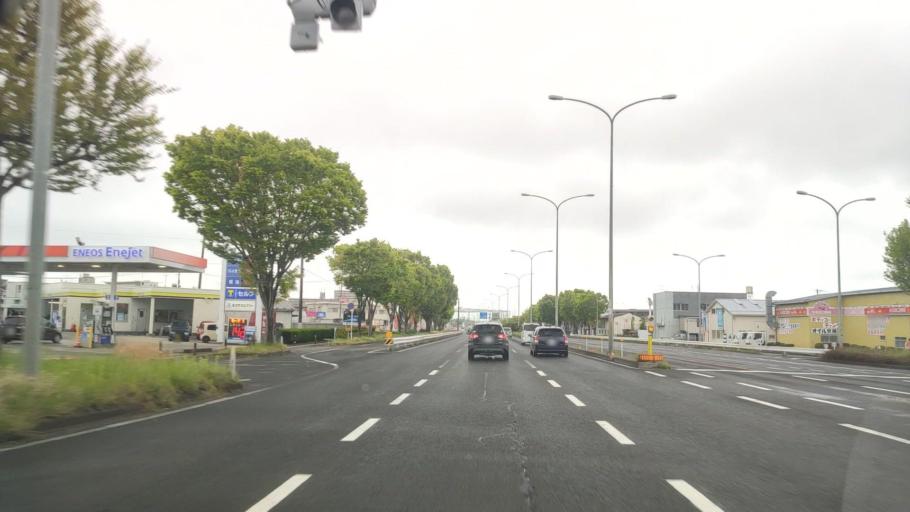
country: JP
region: Miyagi
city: Sendai
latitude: 38.2401
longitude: 140.9181
